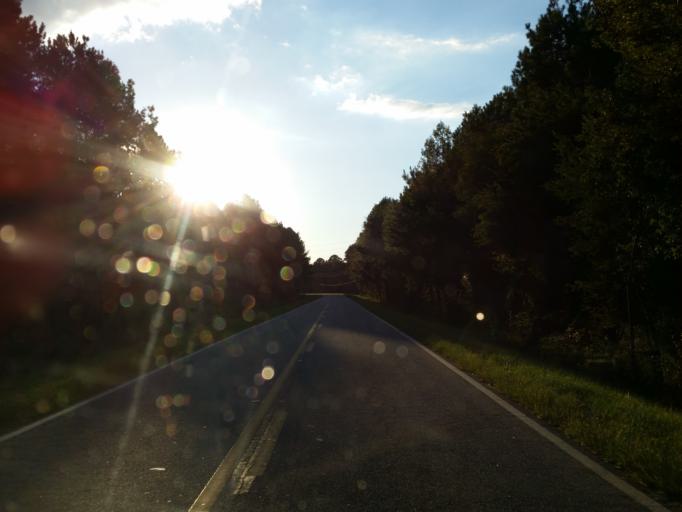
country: US
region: Georgia
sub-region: Crisp County
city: Cordele
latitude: 32.0061
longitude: -83.7414
